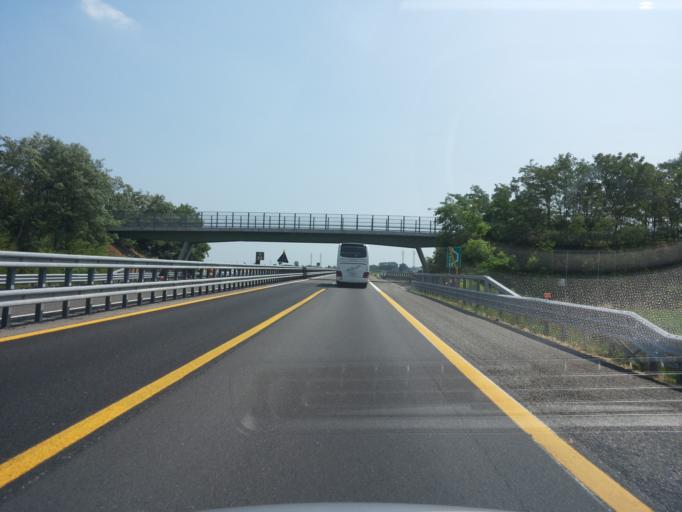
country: IT
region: Lombardy
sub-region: Provincia di Pavia
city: Voghera
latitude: 45.0170
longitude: 9.0201
